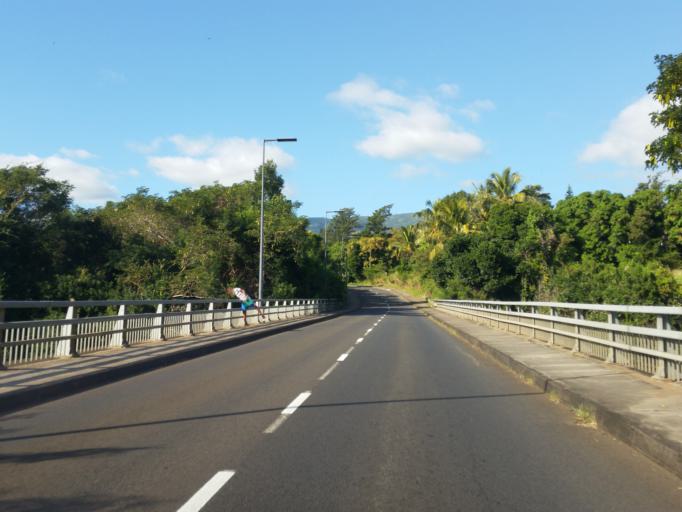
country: RE
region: Reunion
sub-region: Reunion
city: Sainte-Marie
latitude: -20.9106
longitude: 55.5018
